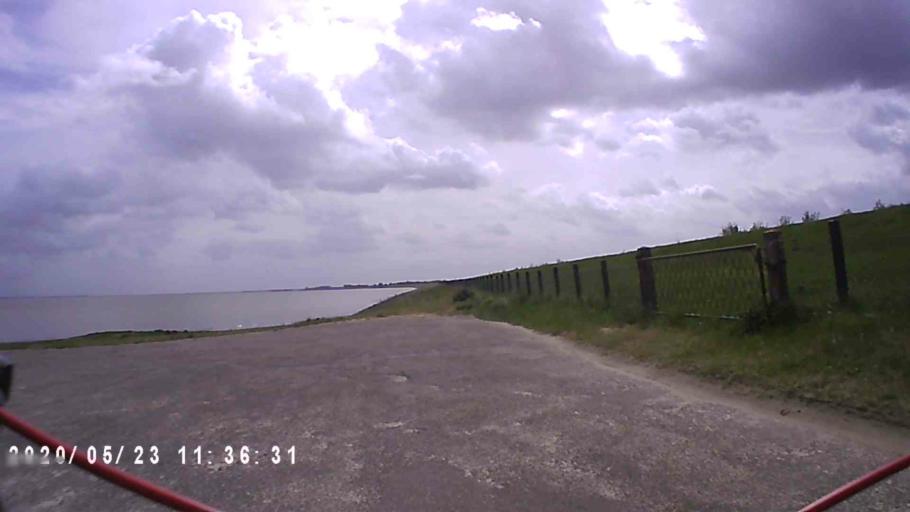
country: NL
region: Groningen
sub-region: Gemeente Delfzijl
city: Delfzijl
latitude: 53.3062
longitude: 7.0091
